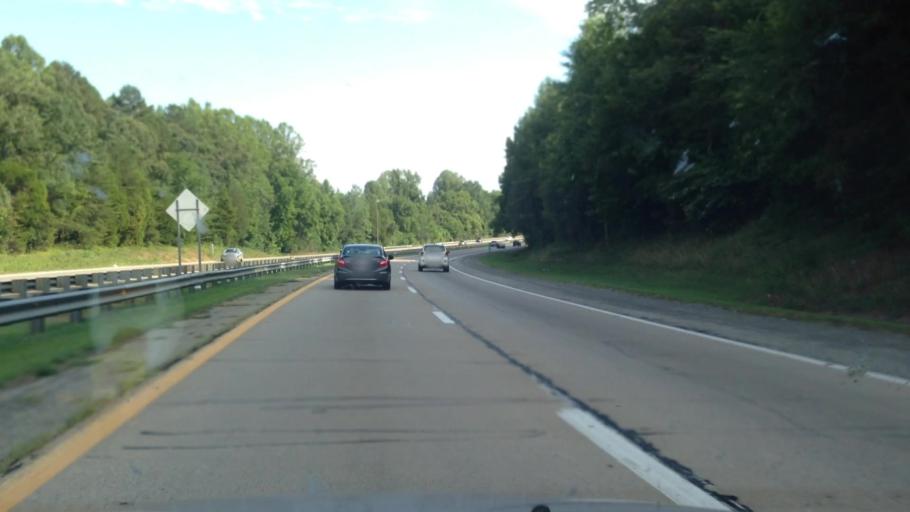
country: US
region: North Carolina
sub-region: Forsyth County
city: Winston-Salem
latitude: 36.0315
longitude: -80.2374
